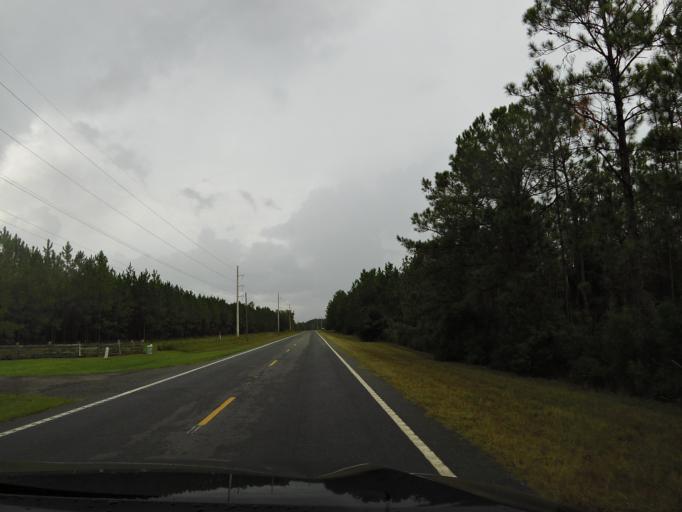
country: US
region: Florida
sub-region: Duval County
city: Baldwin
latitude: 30.4945
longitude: -82.0388
